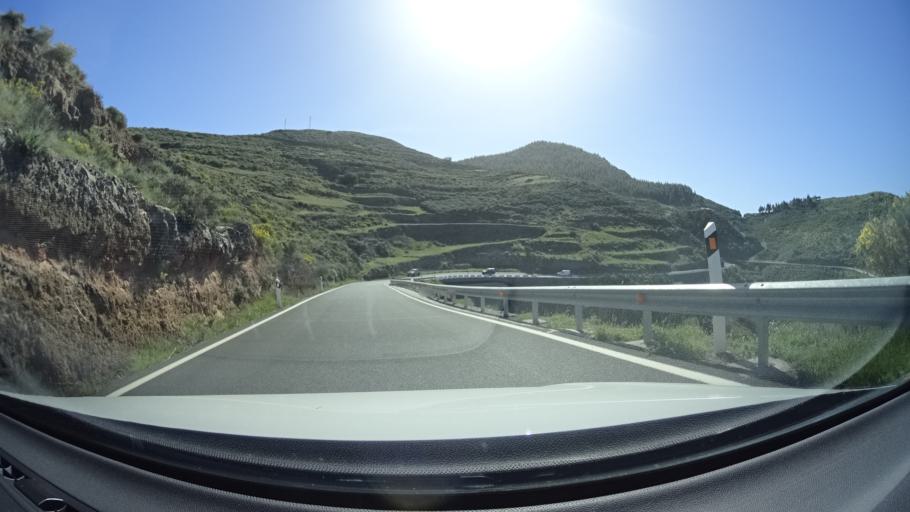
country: ES
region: Canary Islands
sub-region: Provincia de Las Palmas
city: Artenara
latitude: 28.0240
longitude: -15.6440
